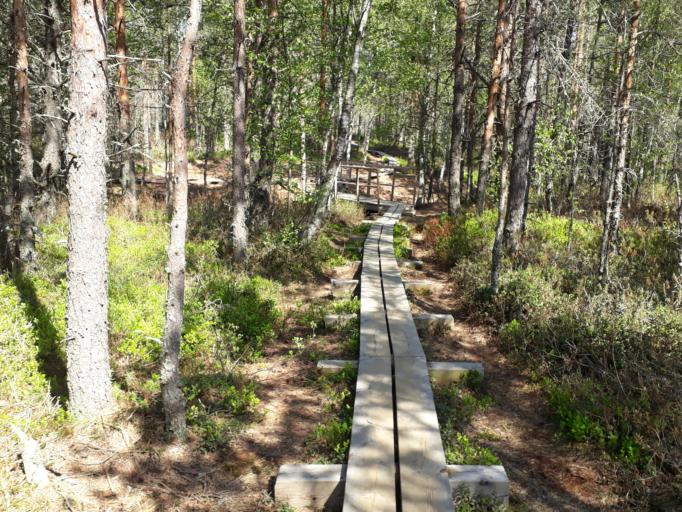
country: EE
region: Harju
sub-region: Loksa linn
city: Loksa
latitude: 59.4771
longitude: 25.6664
